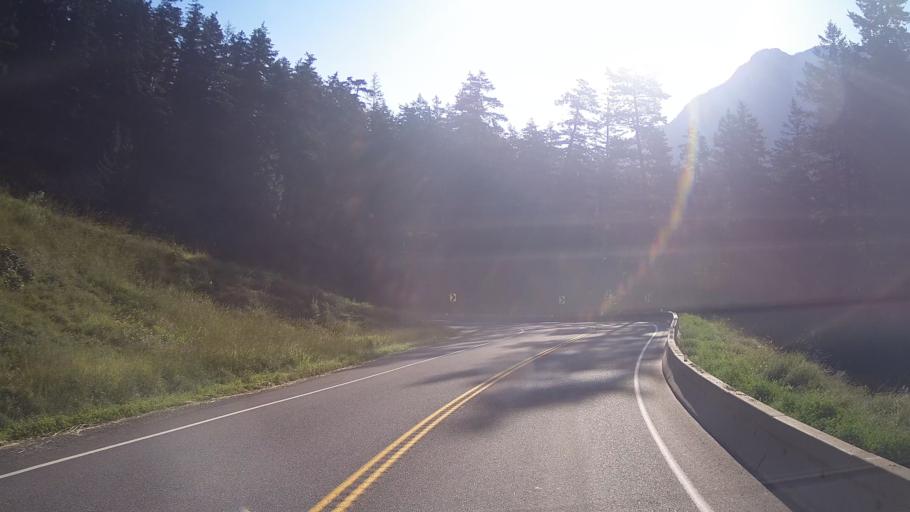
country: CA
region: British Columbia
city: Lillooet
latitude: 50.6546
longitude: -122.0091
